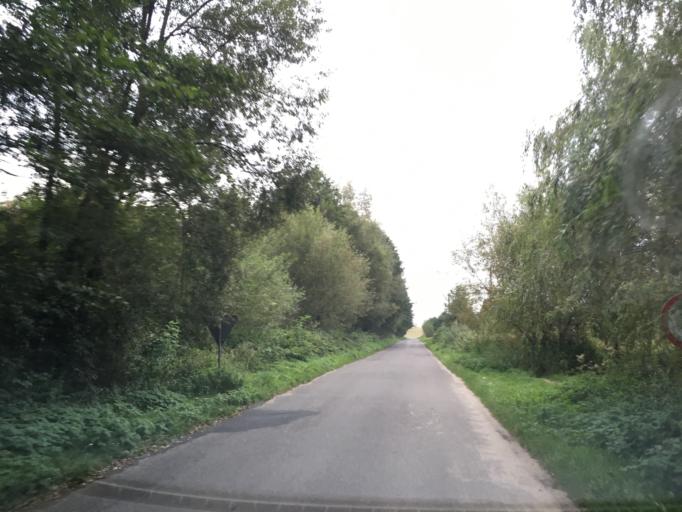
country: PL
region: Lodz Voivodeship
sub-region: Powiat piotrkowski
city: Leki Szlacheckie
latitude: 51.2107
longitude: 19.7210
